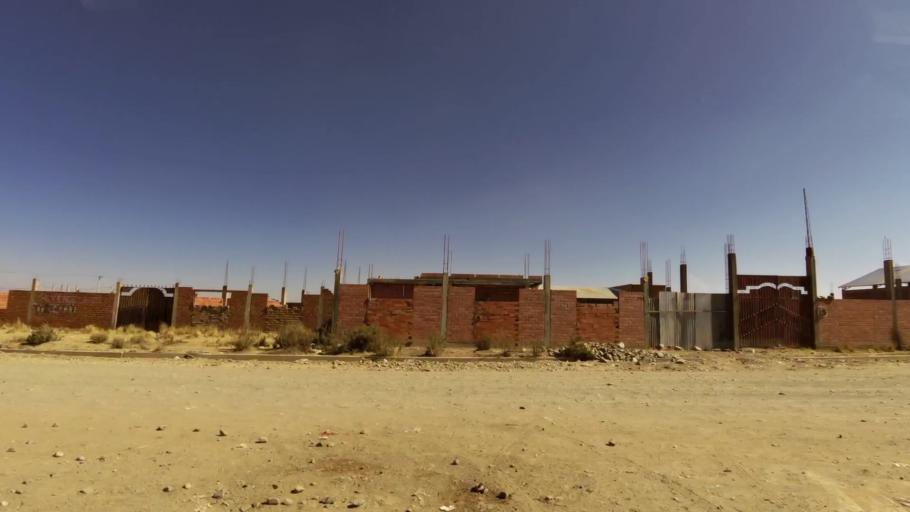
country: BO
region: La Paz
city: La Paz
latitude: -16.6006
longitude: -68.2018
